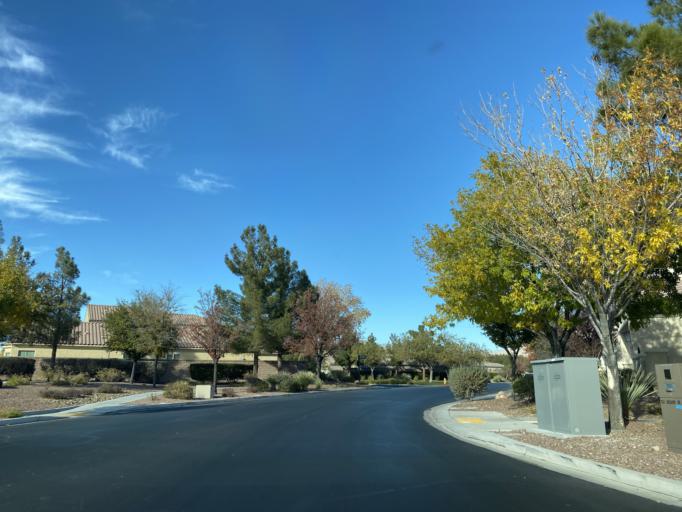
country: US
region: Nevada
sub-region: Clark County
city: North Las Vegas
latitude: 36.3187
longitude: -115.2518
